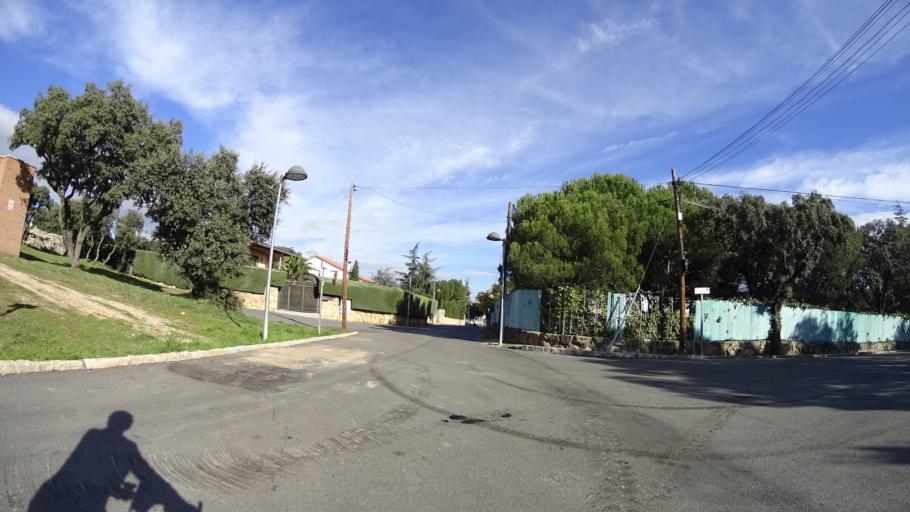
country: ES
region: Madrid
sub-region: Provincia de Madrid
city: Galapagar
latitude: 40.5822
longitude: -4.0234
